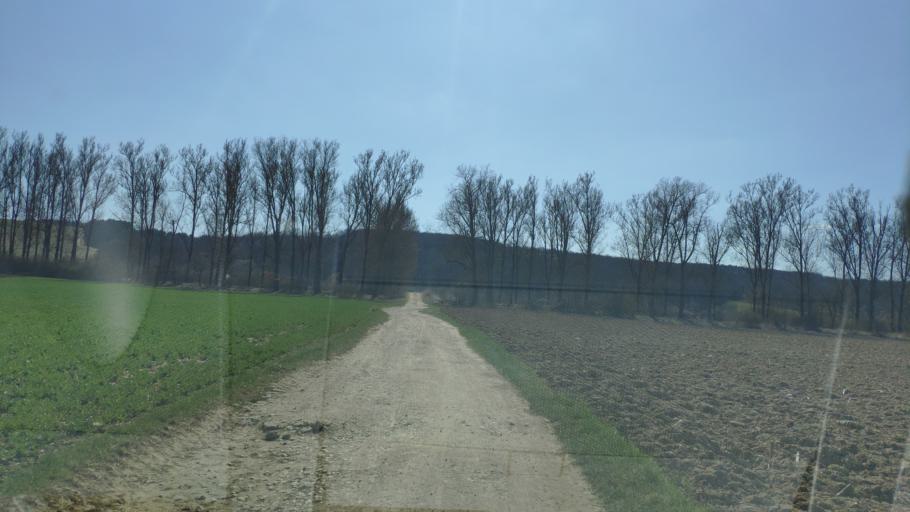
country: SK
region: Kosicky
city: Moldava nad Bodvou
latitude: 48.5703
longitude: 20.9452
